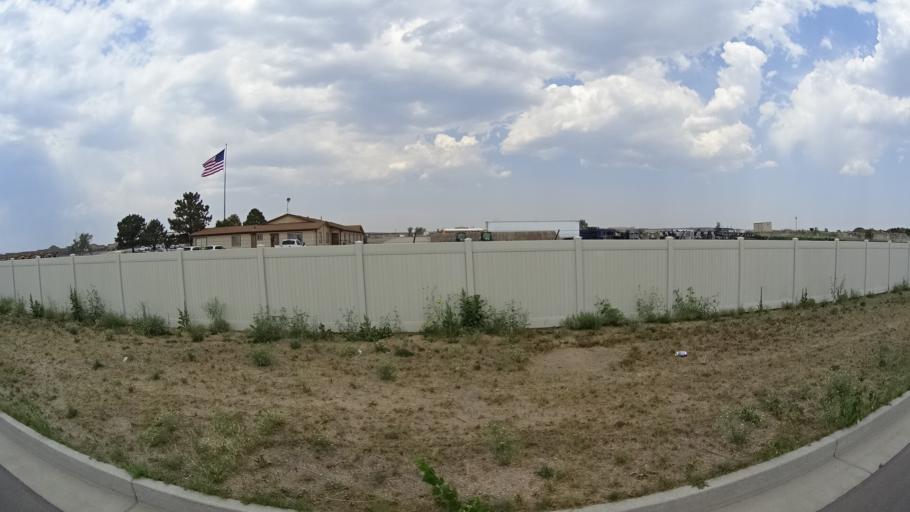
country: US
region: Colorado
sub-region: El Paso County
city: Black Forest
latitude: 38.9482
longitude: -104.6874
